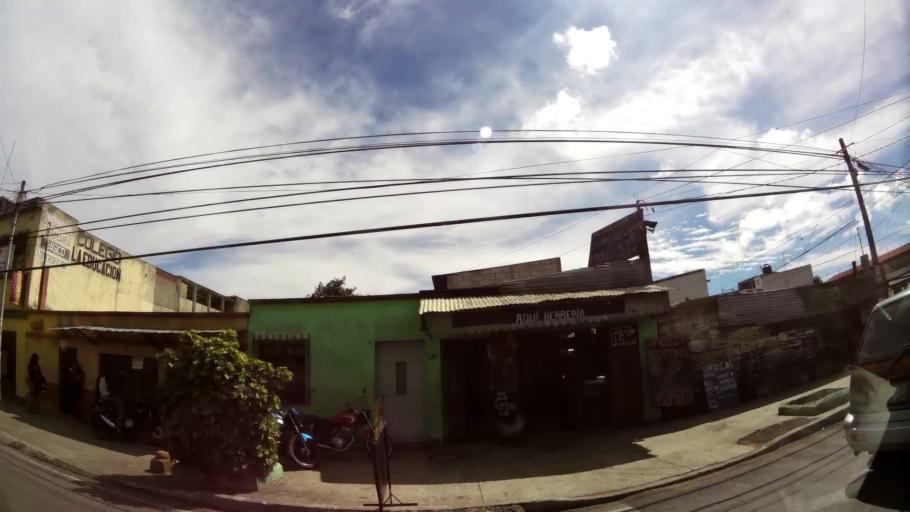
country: GT
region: Guatemala
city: Mixco
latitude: 14.6555
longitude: -90.5817
